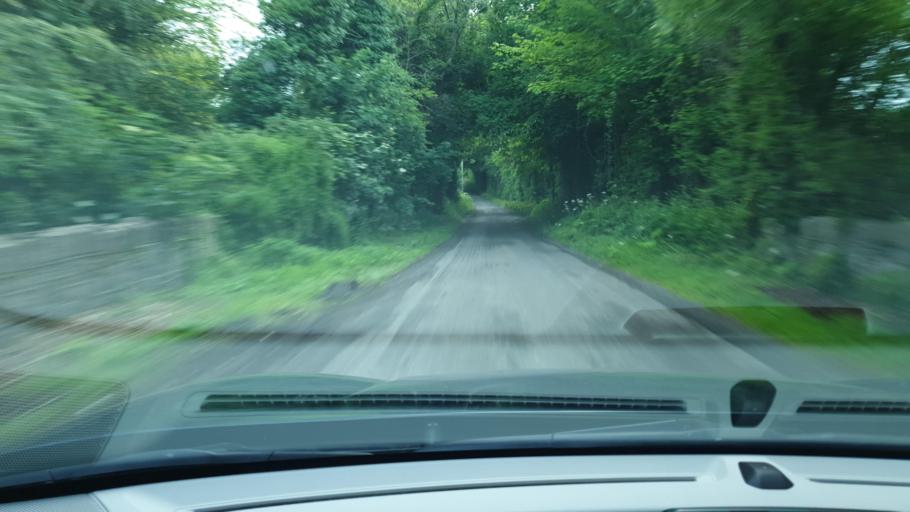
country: IE
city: Kentstown
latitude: 53.5777
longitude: -6.5187
